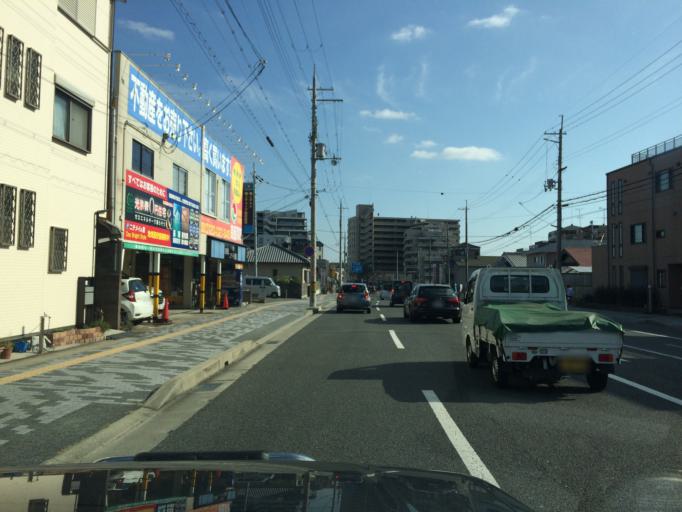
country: JP
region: Hyogo
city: Itami
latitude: 34.7805
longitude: 135.3980
